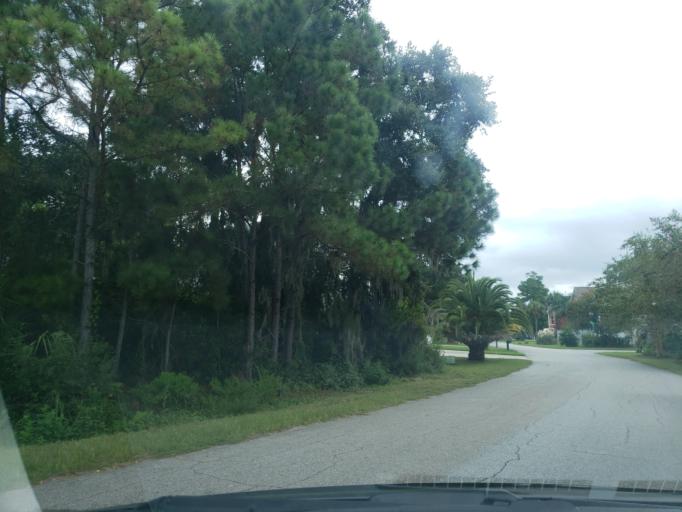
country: US
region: Georgia
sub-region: Chatham County
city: Wilmington Island
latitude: 32.0091
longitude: -80.9565
